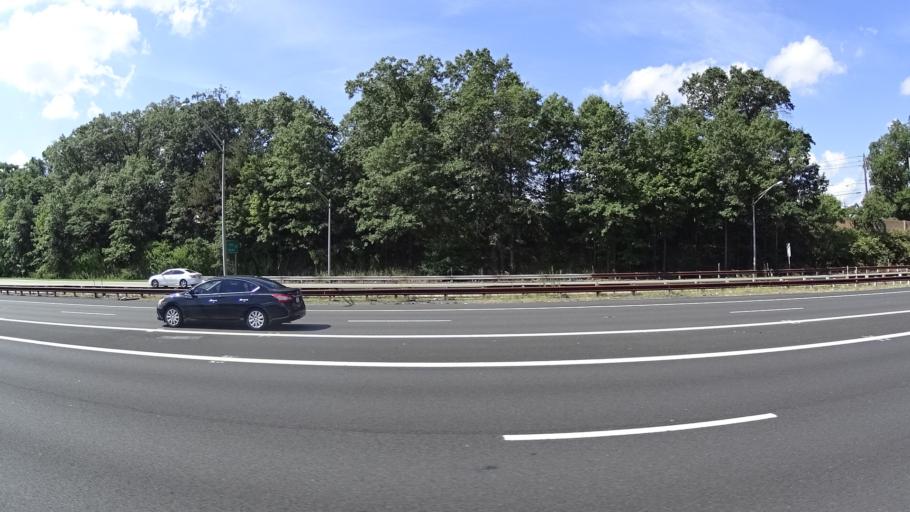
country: US
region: New Jersey
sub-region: Middlesex County
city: Fords
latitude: 40.5359
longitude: -74.3035
